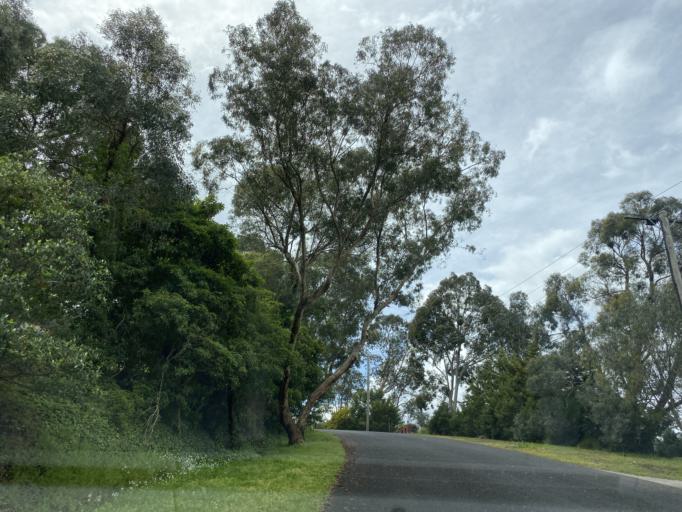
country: AU
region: Victoria
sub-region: Banyule
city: Darch
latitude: -37.7461
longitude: 145.1174
